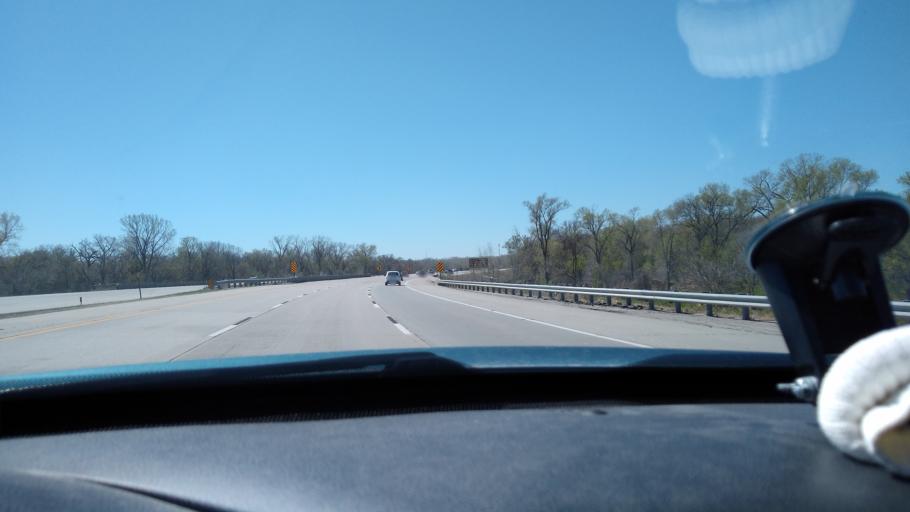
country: US
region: Nebraska
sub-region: Saunders County
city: Ashland
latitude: 41.0336
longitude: -96.2919
